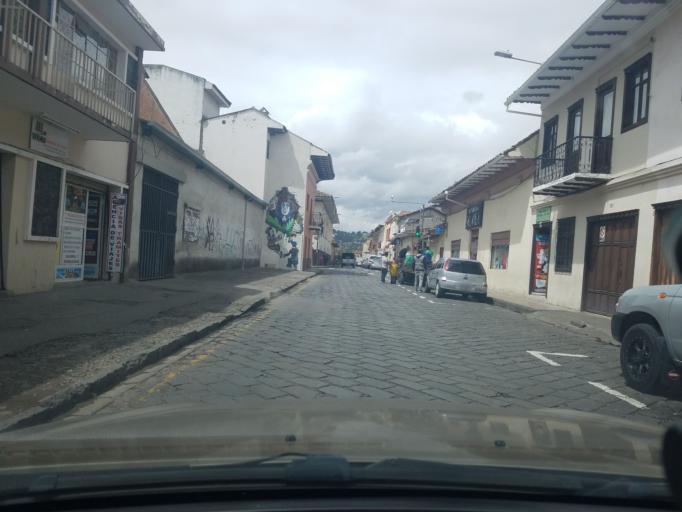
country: EC
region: Azuay
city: Cuenca
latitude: -2.8983
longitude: -79.0010
